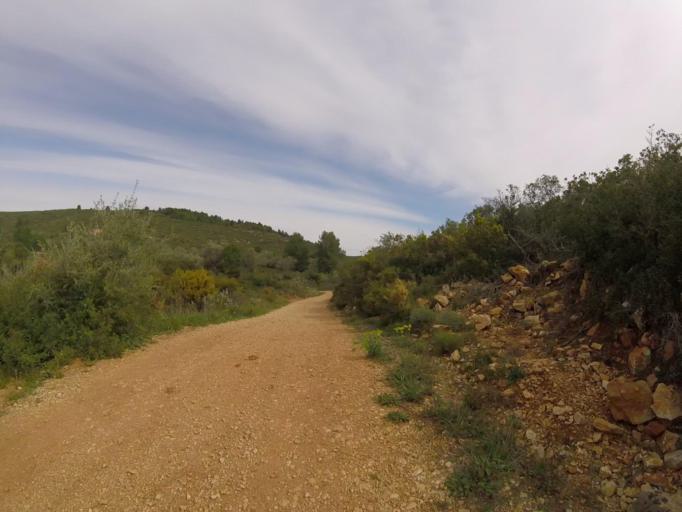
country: ES
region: Valencia
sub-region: Provincia de Castello
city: Cabanes
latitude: 40.1913
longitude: 0.1104
